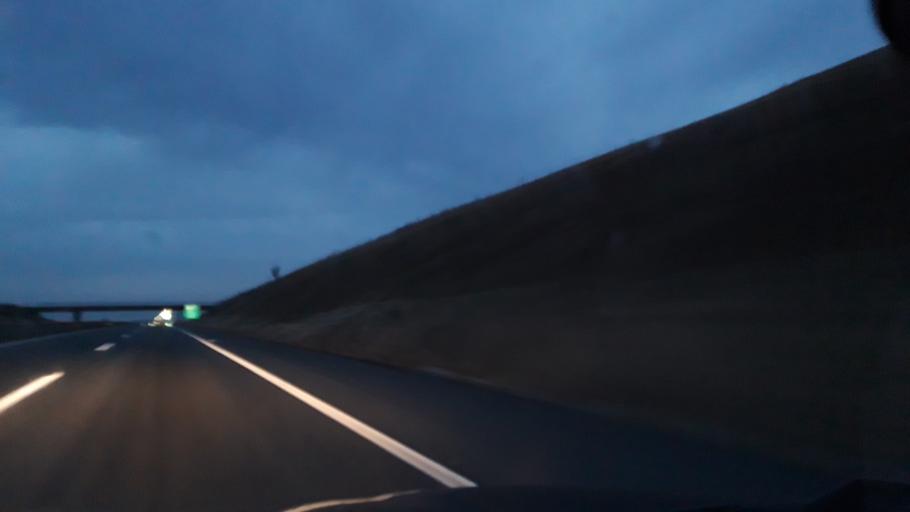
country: RS
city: Beska
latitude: 45.1566
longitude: 20.0818
